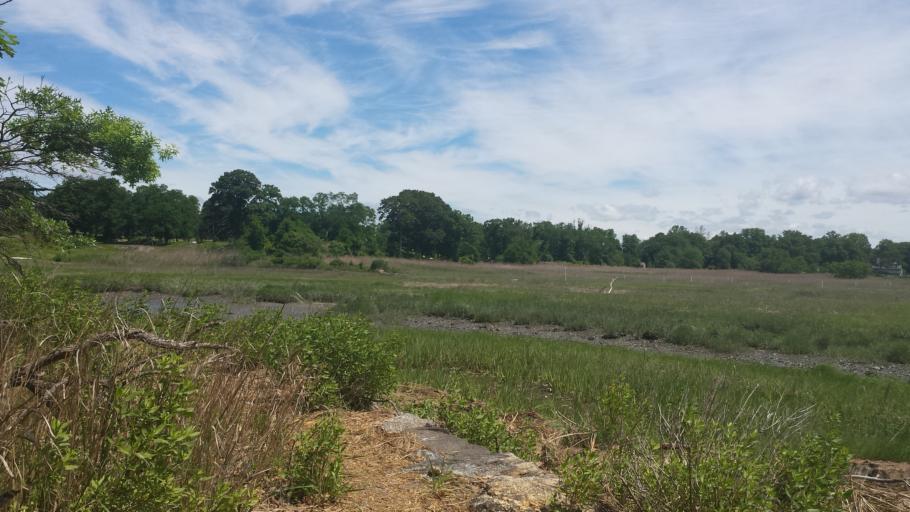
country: US
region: New York
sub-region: Westchester County
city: Harrison
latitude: 40.9537
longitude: -73.6973
